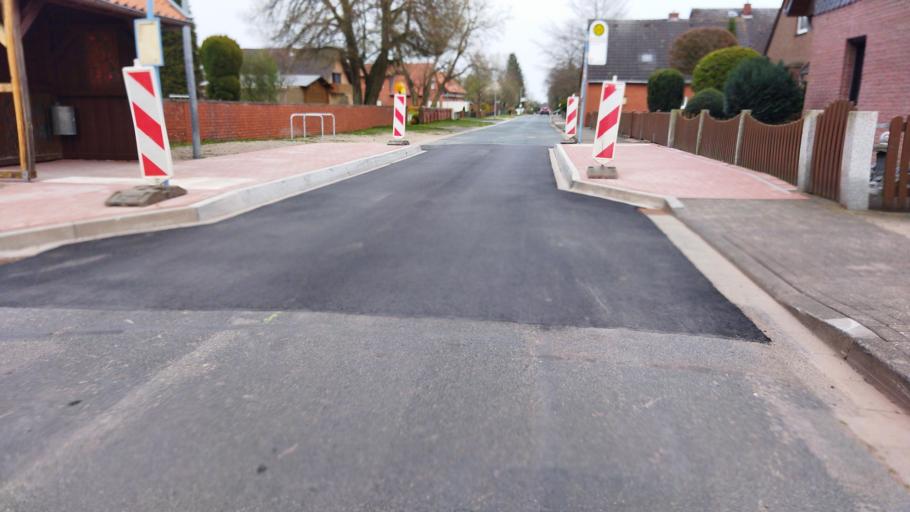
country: DE
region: Lower Saxony
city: Estorf
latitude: 52.5971
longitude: 9.1551
